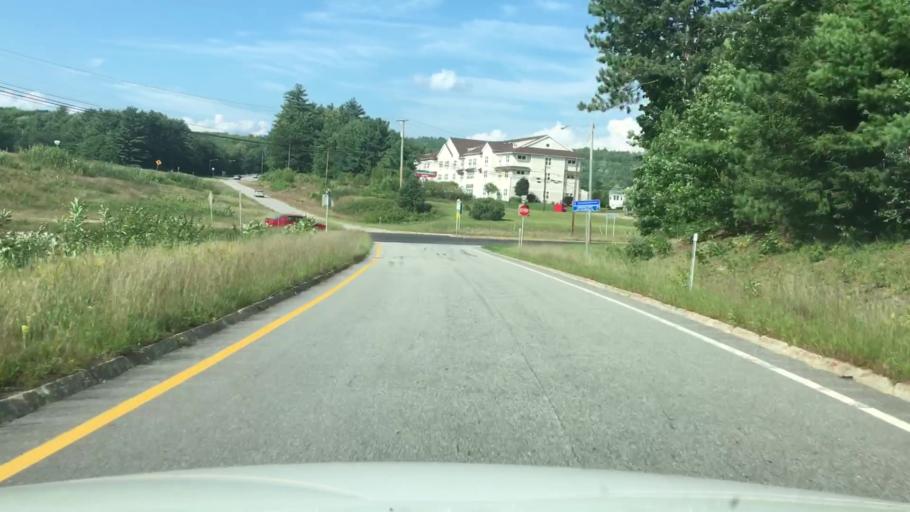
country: US
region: New Hampshire
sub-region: Belknap County
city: Laconia
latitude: 43.5307
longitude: -71.4417
